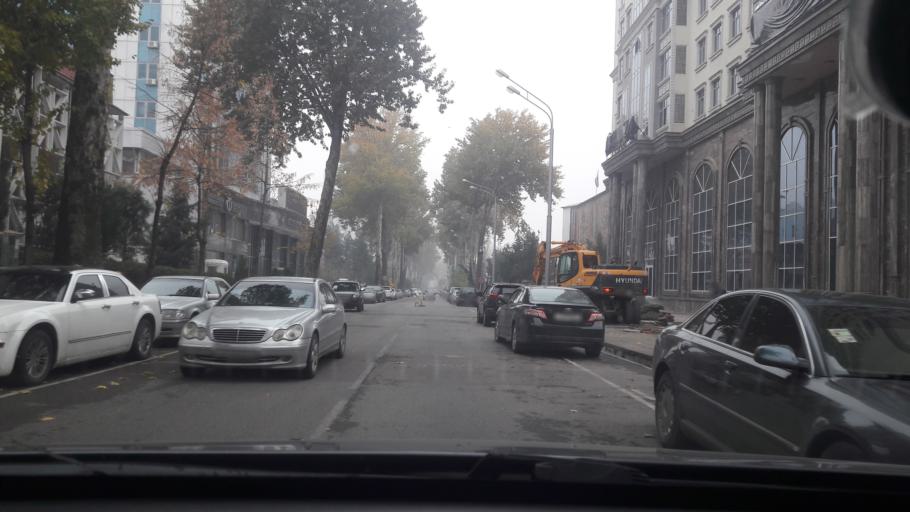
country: TJ
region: Dushanbe
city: Dushanbe
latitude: 38.5782
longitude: 68.7894
